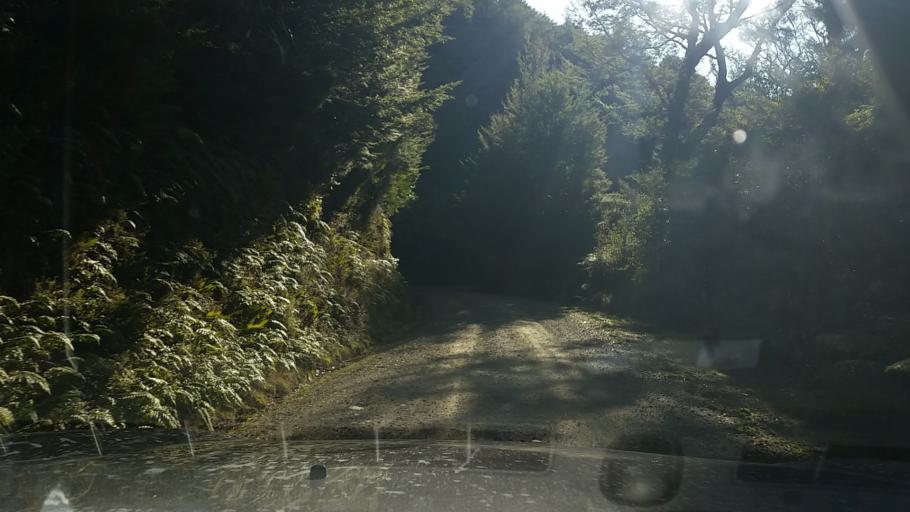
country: NZ
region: Marlborough
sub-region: Marlborough District
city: Picton
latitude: -41.0595
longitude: 174.1582
